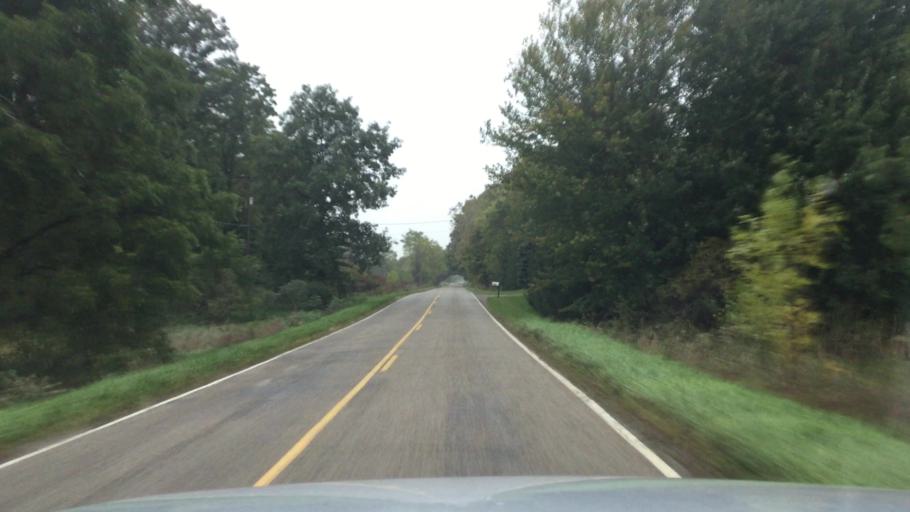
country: US
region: Michigan
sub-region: Shiawassee County
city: Owosso
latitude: 42.9371
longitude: -84.1696
